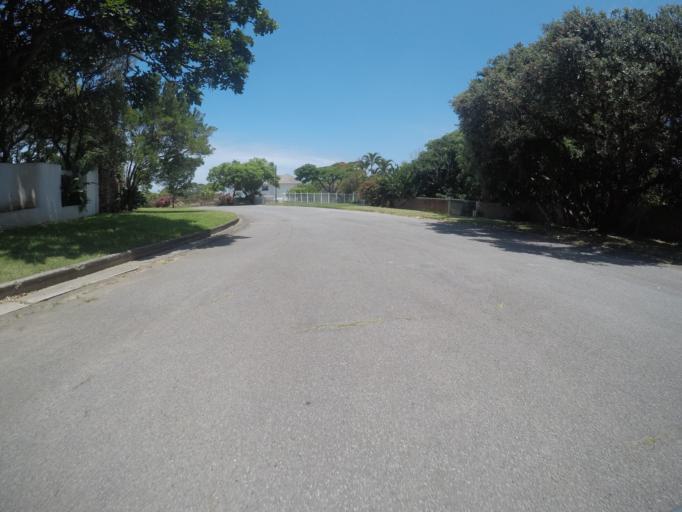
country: ZA
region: Eastern Cape
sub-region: Buffalo City Metropolitan Municipality
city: East London
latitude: -32.9987
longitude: 27.9254
